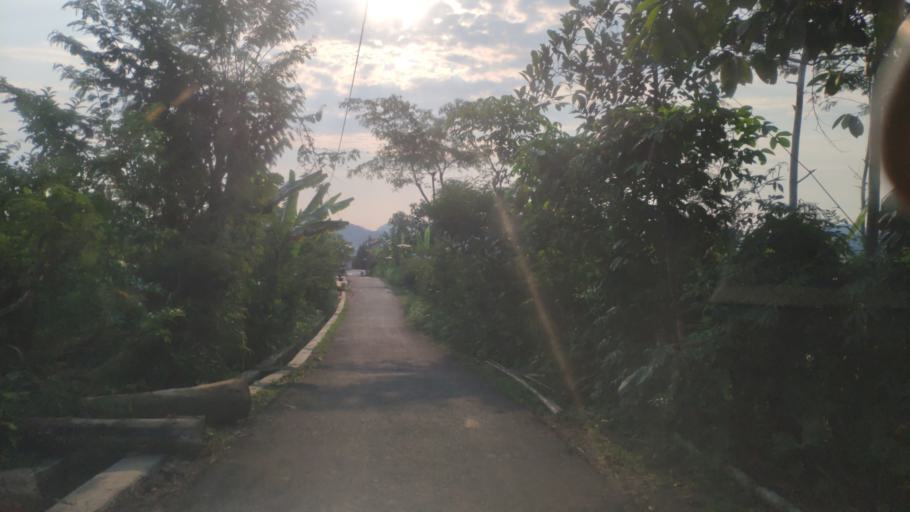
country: ID
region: Central Java
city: Wonosobo
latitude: -7.2634
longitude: 109.6841
